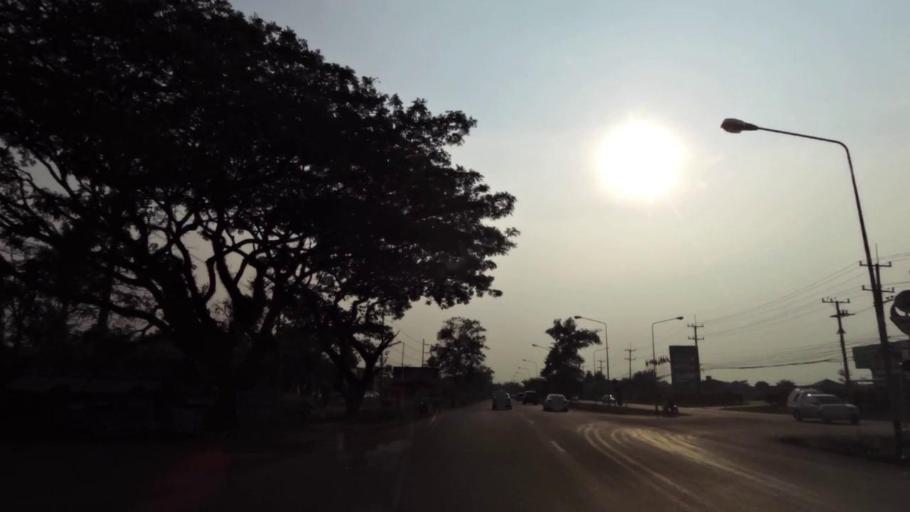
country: TH
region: Chanthaburi
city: Chanthaburi
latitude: 12.6111
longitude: 102.1363
